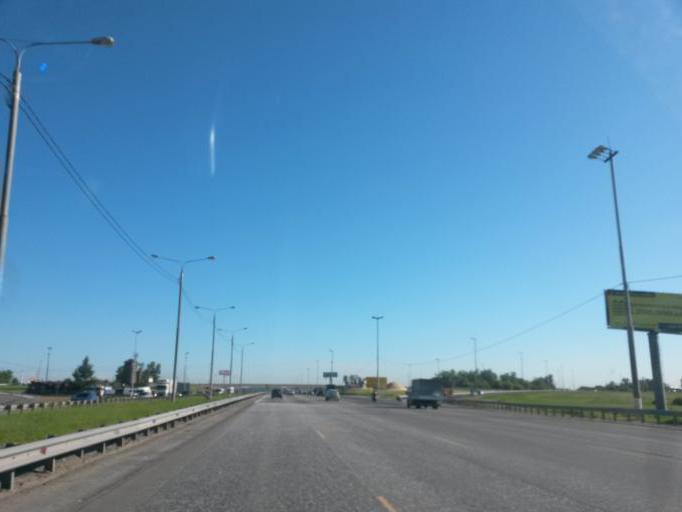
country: RU
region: Moskovskaya
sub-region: Podol'skiy Rayon
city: Podol'sk
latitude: 55.4329
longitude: 37.6150
